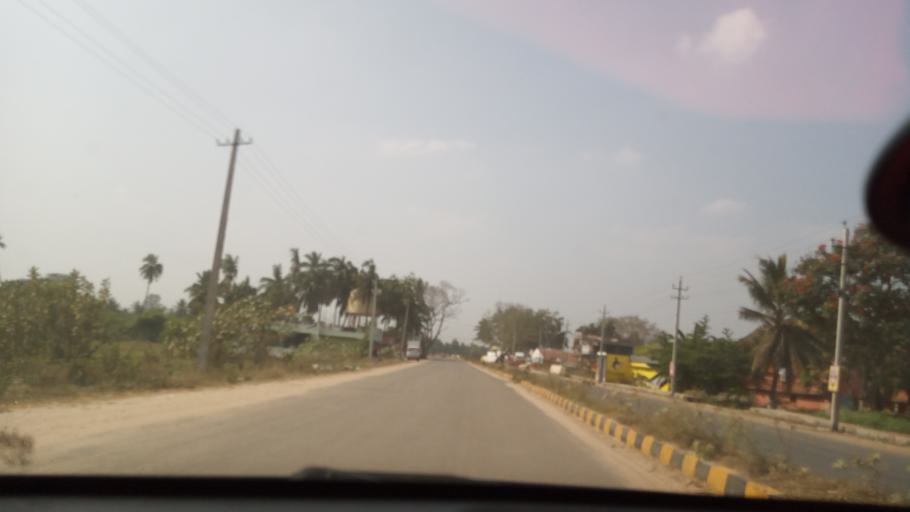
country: IN
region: Karnataka
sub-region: Mysore
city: Nanjangud
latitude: 12.1120
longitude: 76.7034
